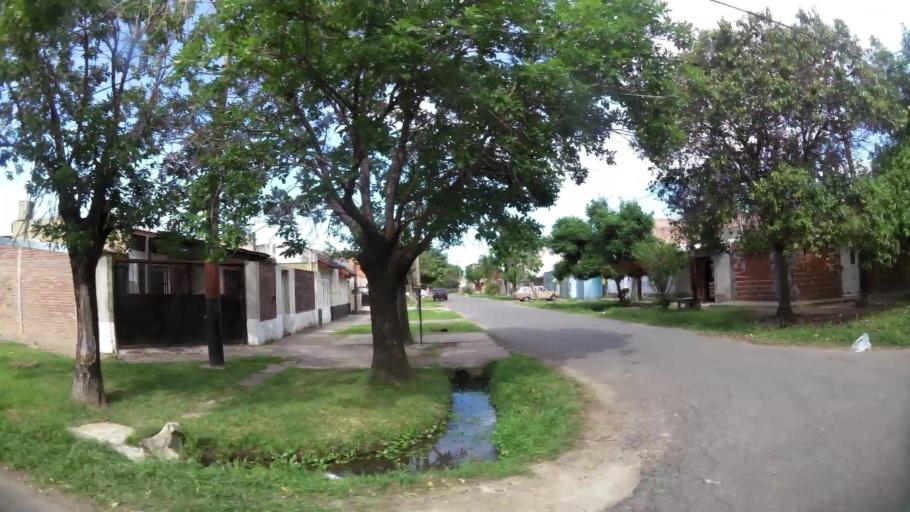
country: AR
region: Santa Fe
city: Granadero Baigorria
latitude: -32.9225
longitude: -60.7158
